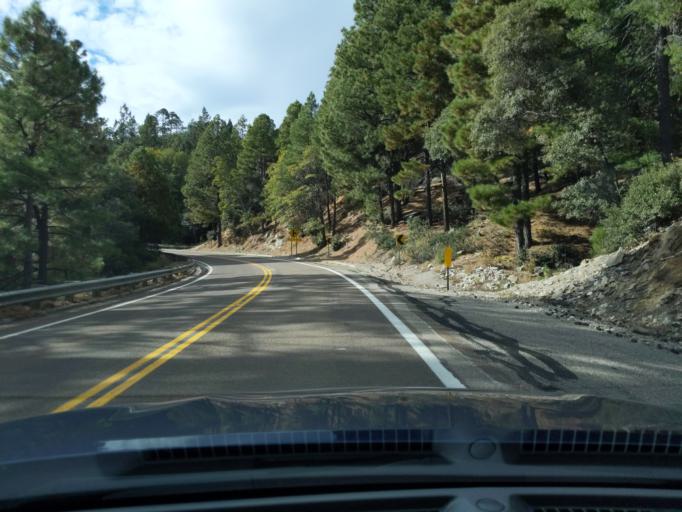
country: US
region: Arizona
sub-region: Pima County
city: Tanque Verde
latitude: 32.4100
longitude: -110.7075
